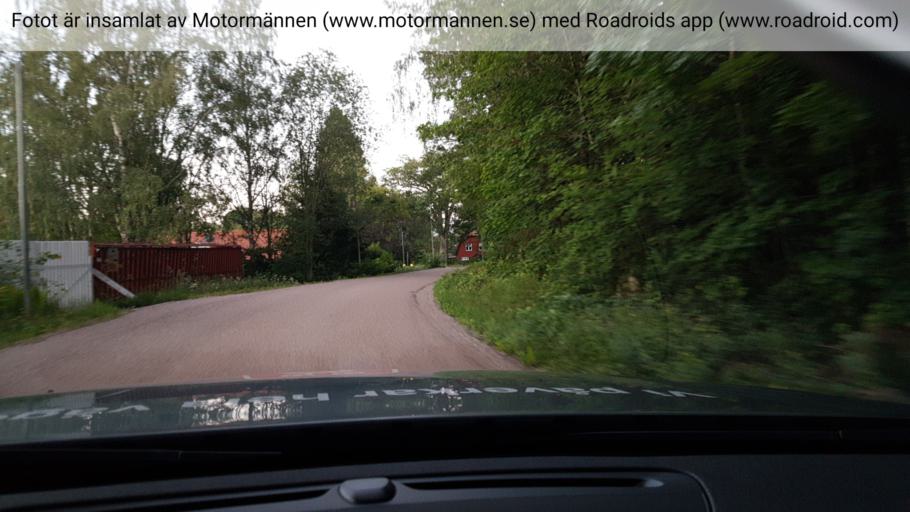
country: SE
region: Vaestmanland
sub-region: Hallstahammars Kommun
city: Kolback
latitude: 59.5280
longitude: 16.2328
